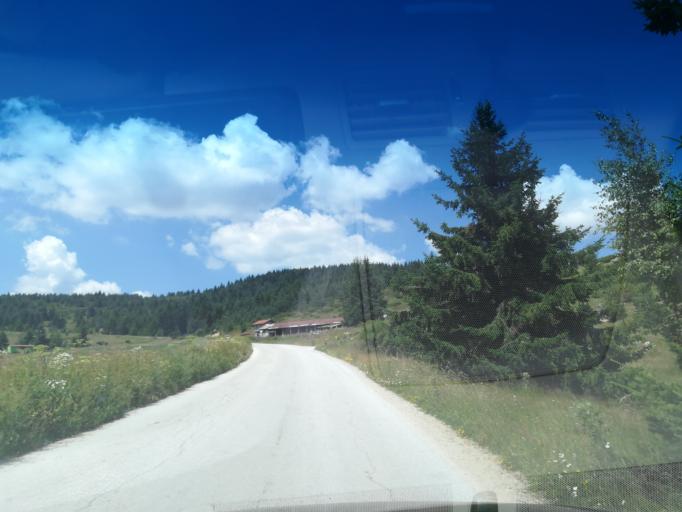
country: BG
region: Smolyan
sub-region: Obshtina Chepelare
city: Chepelare
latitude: 41.6962
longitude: 24.7817
